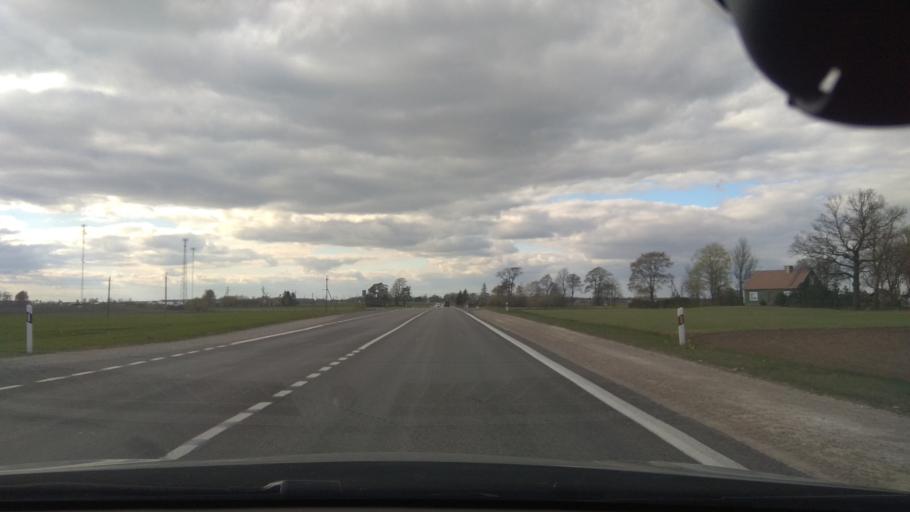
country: LT
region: Siauliu apskritis
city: Pakruojis
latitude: 55.7872
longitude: 24.0363
